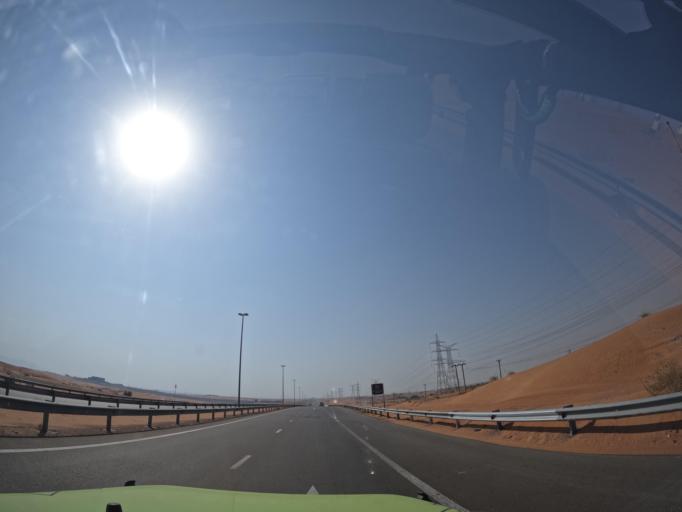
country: OM
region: Al Buraimi
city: Al Buraymi
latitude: 24.3471
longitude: 55.7388
